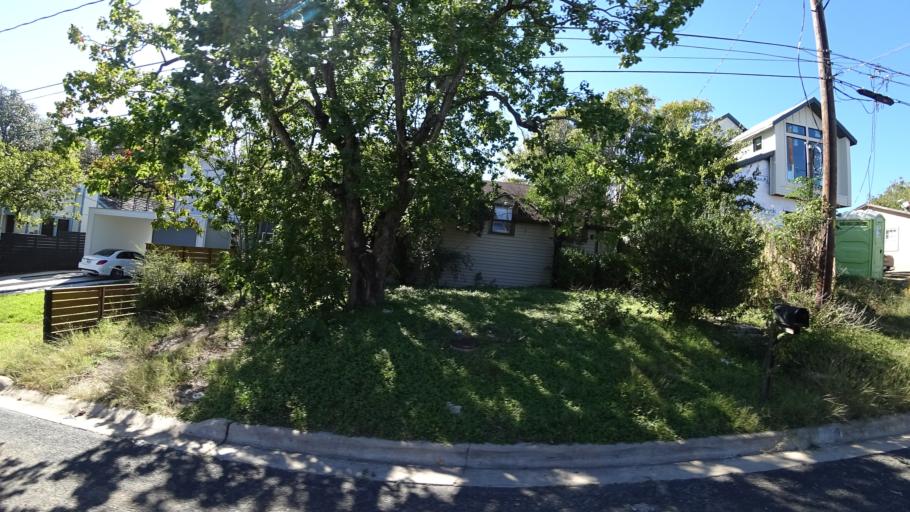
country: US
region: Texas
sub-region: Travis County
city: Austin
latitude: 30.2828
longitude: -97.6928
